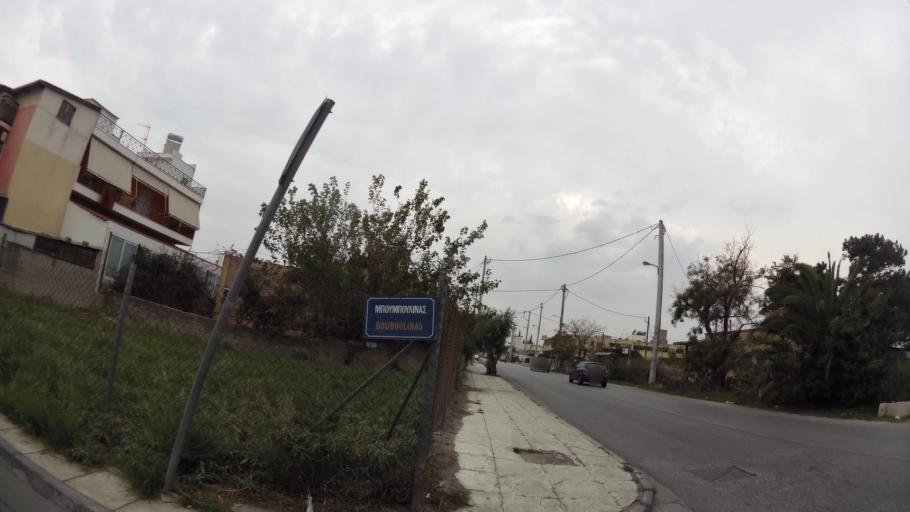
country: GR
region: Attica
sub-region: Nomarchia Athinas
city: Tavros
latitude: 37.9723
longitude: 23.6808
